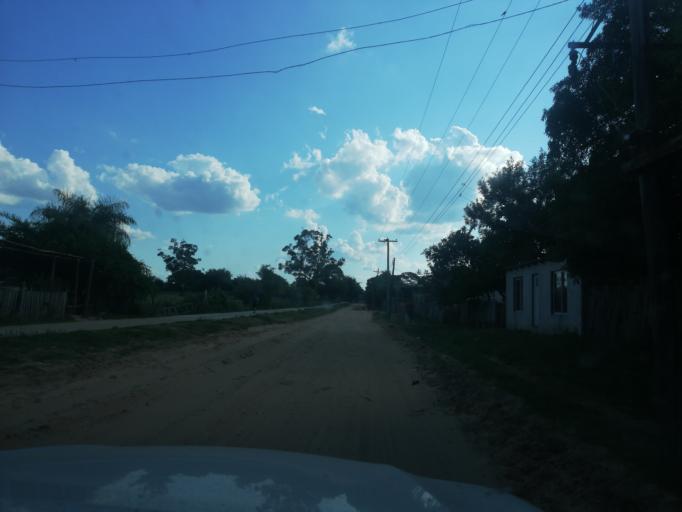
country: AR
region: Corrientes
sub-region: Departamento de San Miguel
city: San Miguel
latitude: -28.0019
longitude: -57.5936
